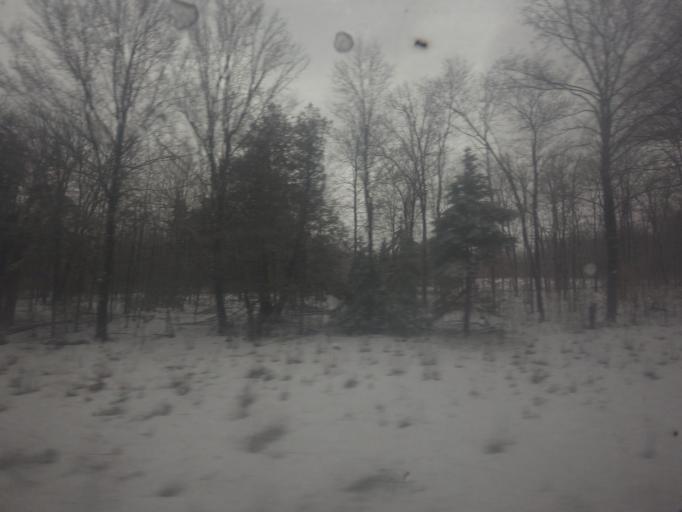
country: CA
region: Ontario
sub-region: Lanark County
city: Smiths Falls
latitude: 44.9840
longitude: -75.9793
